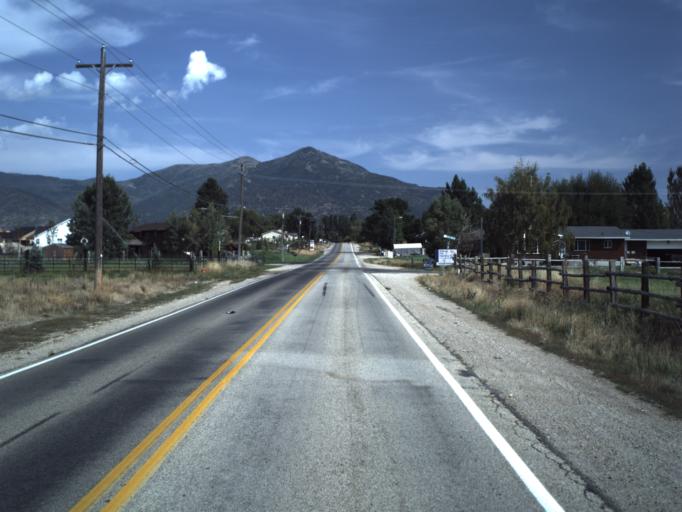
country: US
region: Utah
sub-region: Wasatch County
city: Midway
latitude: 40.4976
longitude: -111.4720
